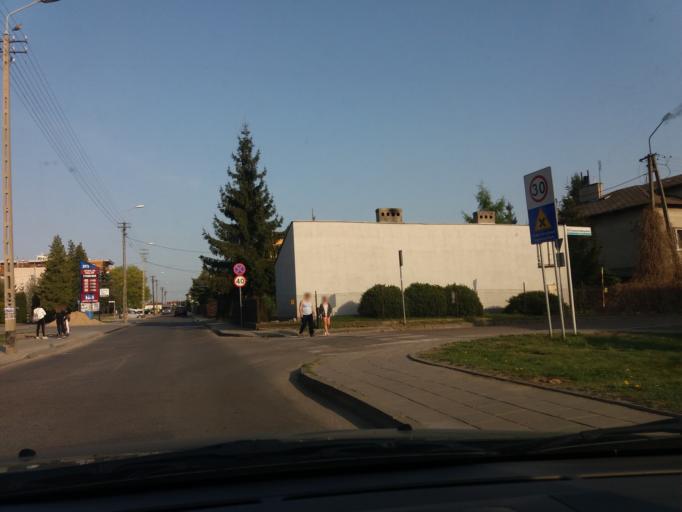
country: PL
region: Masovian Voivodeship
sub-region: Powiat mlawski
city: Mlawa
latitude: 53.1206
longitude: 20.3794
